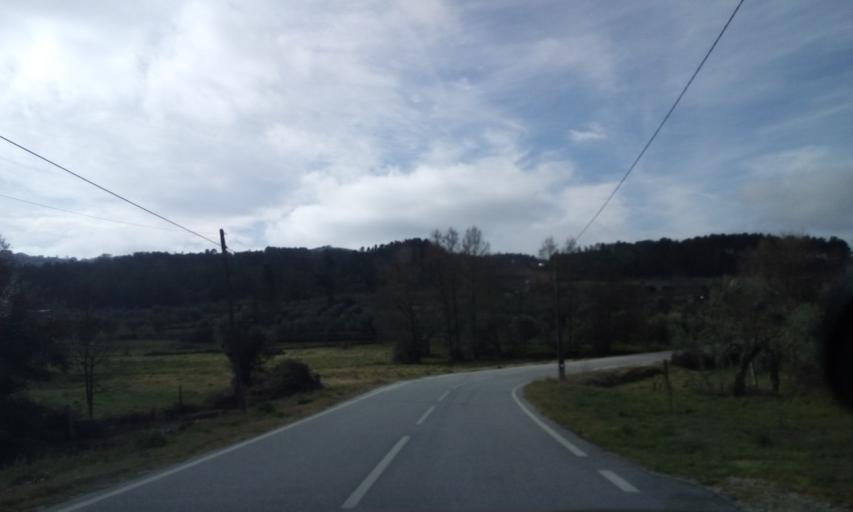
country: PT
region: Guarda
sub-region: Fornos de Algodres
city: Fornos de Algodres
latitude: 40.7024
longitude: -7.5593
